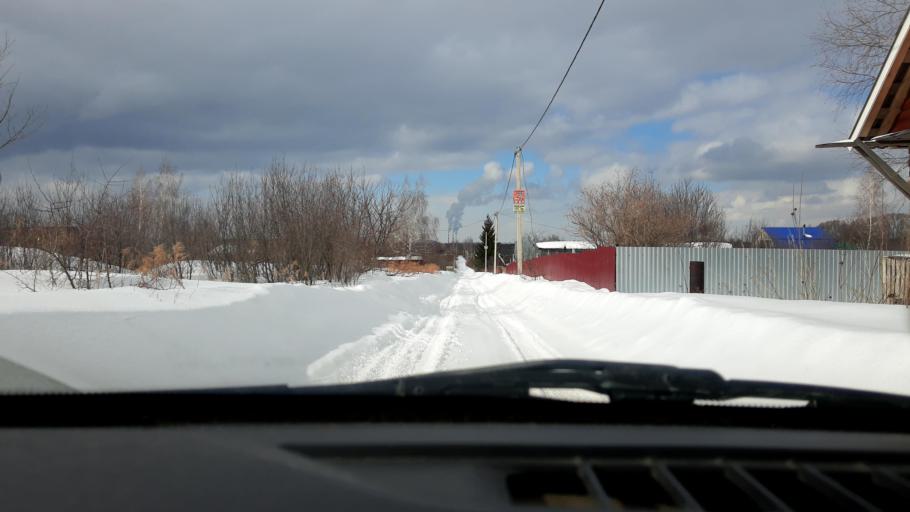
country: RU
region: Bashkortostan
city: Iglino
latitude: 54.7302
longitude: 56.2321
